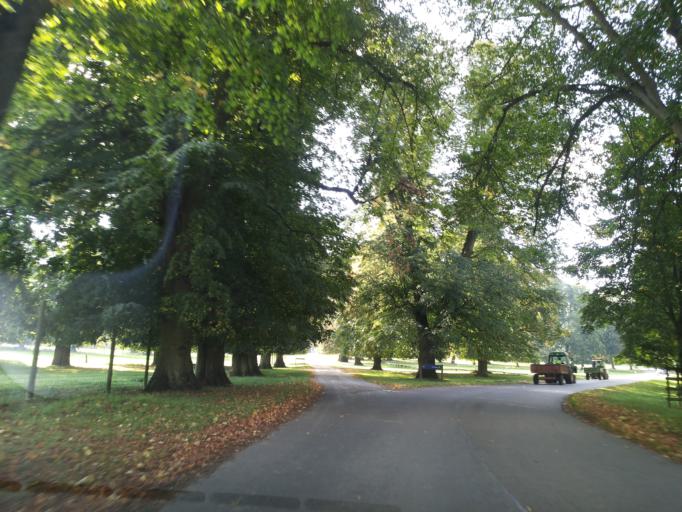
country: GB
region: England
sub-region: Lincolnshire
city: Stamford
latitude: 52.6448
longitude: -0.4464
